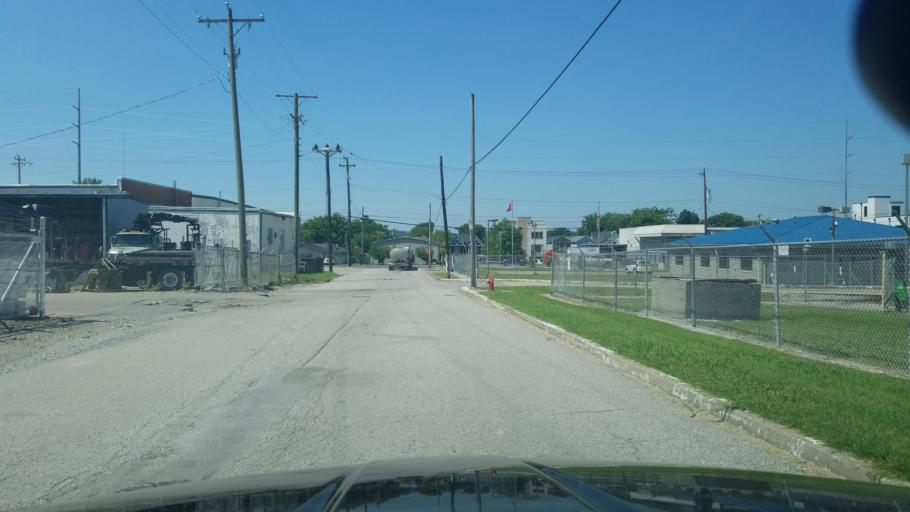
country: US
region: Tennessee
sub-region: Davidson County
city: Belle Meade
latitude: 36.1687
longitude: -86.8588
